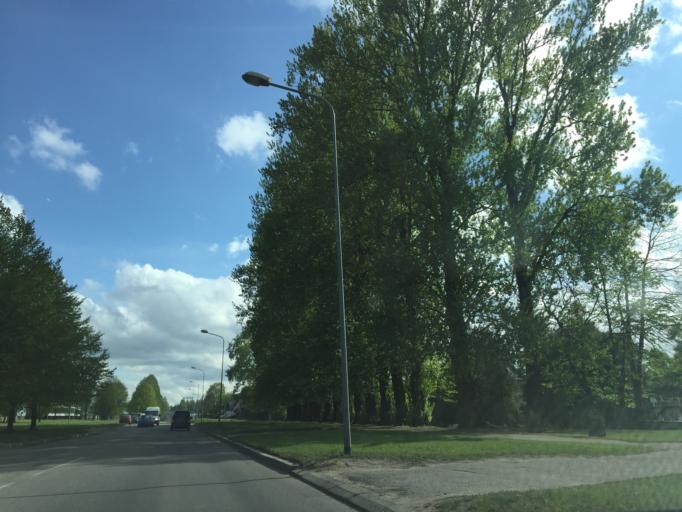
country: LV
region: Riga
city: Riga
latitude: 56.9363
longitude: 24.1951
